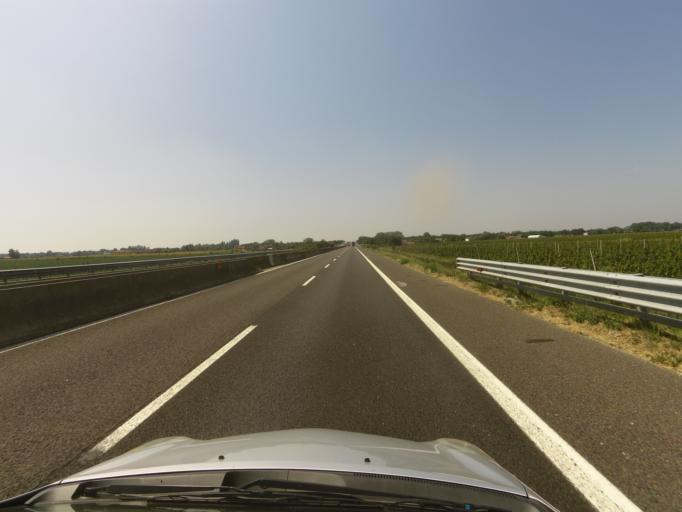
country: IT
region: Veneto
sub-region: Provincia di Rovigo
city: Villamarzana
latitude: 45.0121
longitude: 11.6844
